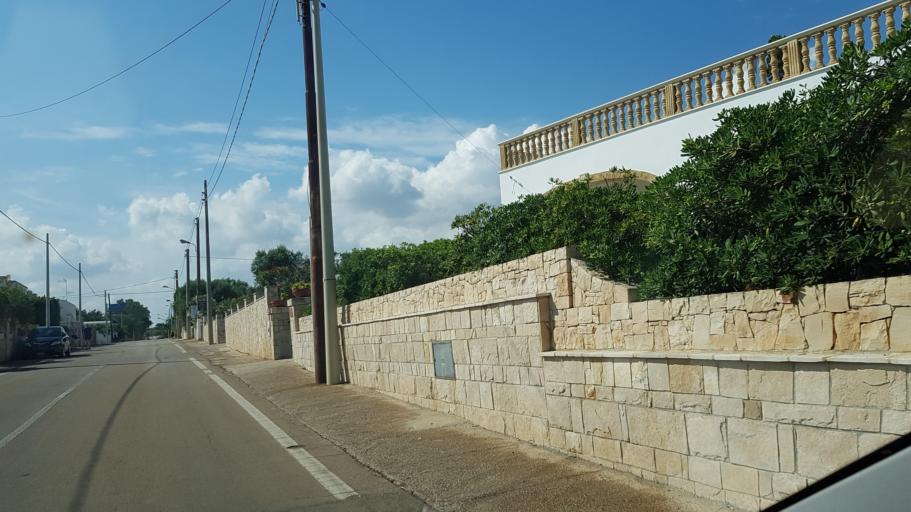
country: IT
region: Apulia
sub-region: Provincia di Lecce
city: Patu
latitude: 39.8117
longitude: 18.3167
